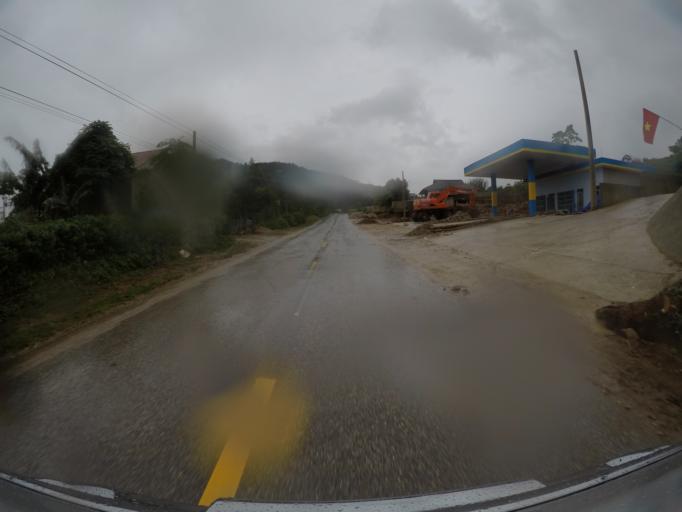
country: VN
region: Lai Chau
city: Than Uyen
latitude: 22.0551
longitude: 103.9028
